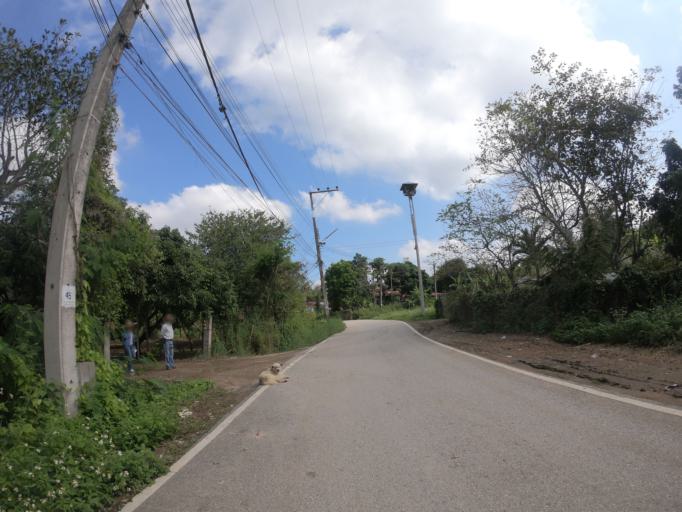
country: TH
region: Chiang Mai
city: Saraphi
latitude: 18.7195
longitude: 99.0170
